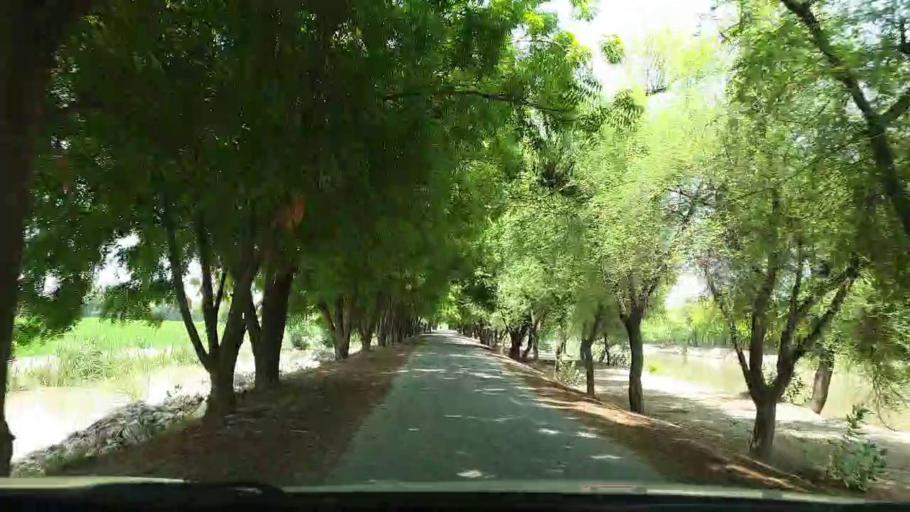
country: PK
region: Sindh
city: Dokri
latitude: 27.3612
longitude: 68.1139
